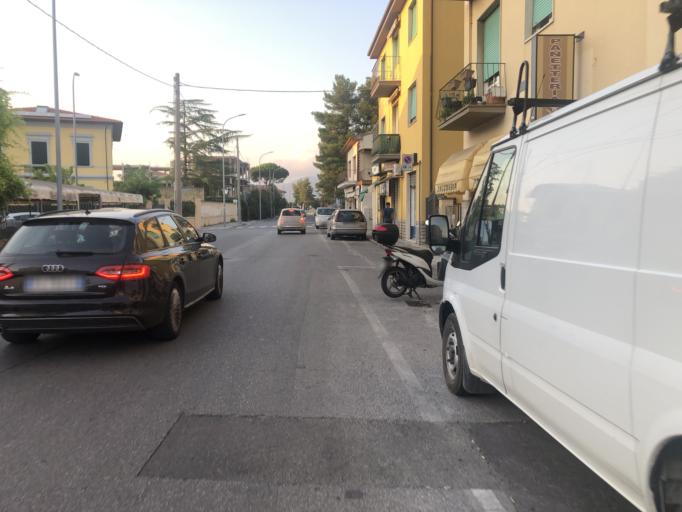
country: IT
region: Tuscany
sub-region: Province of Pisa
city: Pisa
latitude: 43.7284
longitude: 10.4061
